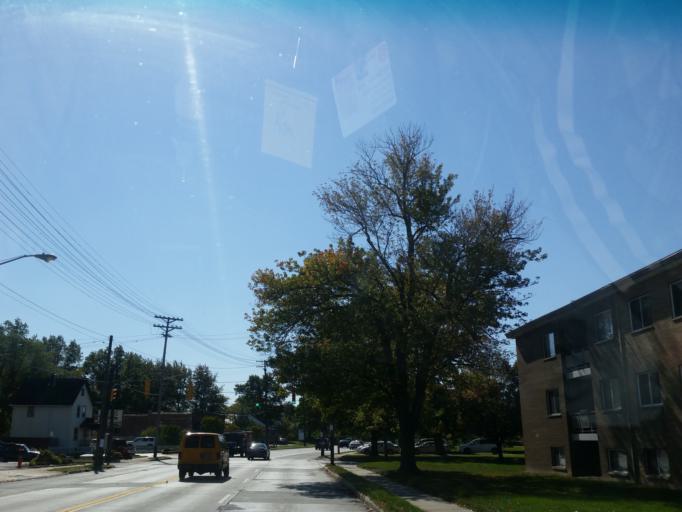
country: US
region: Ohio
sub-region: Cuyahoga County
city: Rocky River
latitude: 41.4376
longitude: -81.8206
